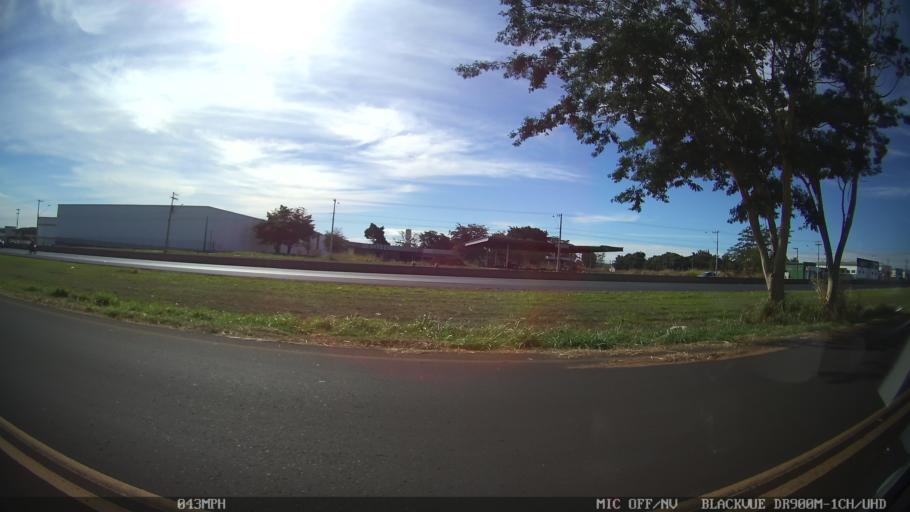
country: BR
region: Sao Paulo
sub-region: Sao Jose Do Rio Preto
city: Sao Jose do Rio Preto
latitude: -20.7935
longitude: -49.3067
